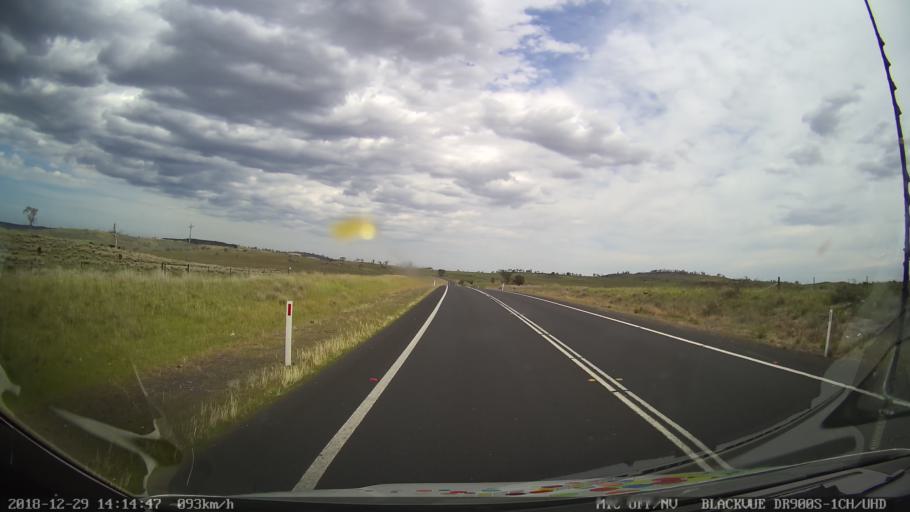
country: AU
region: New South Wales
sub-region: Cooma-Monaro
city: Cooma
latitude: -36.4470
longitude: 149.2365
